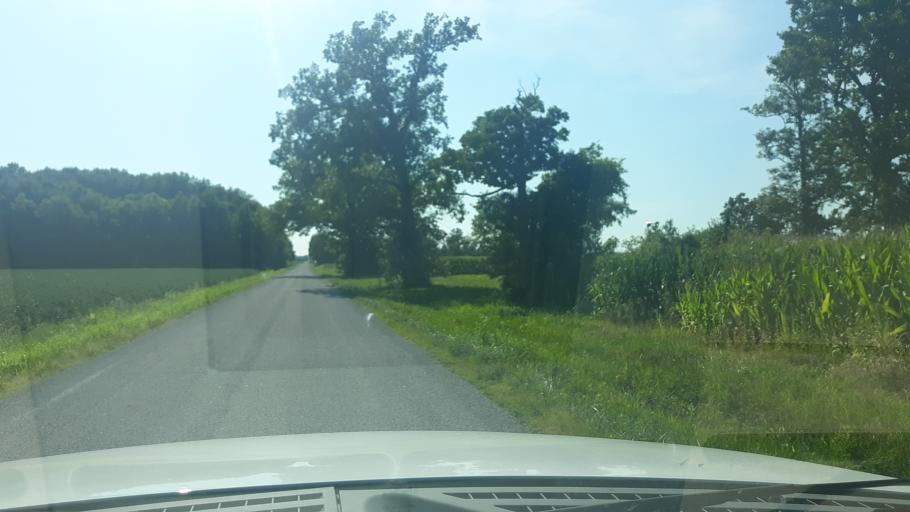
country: US
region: Illinois
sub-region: Saline County
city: Eldorado
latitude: 37.8632
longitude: -88.4874
